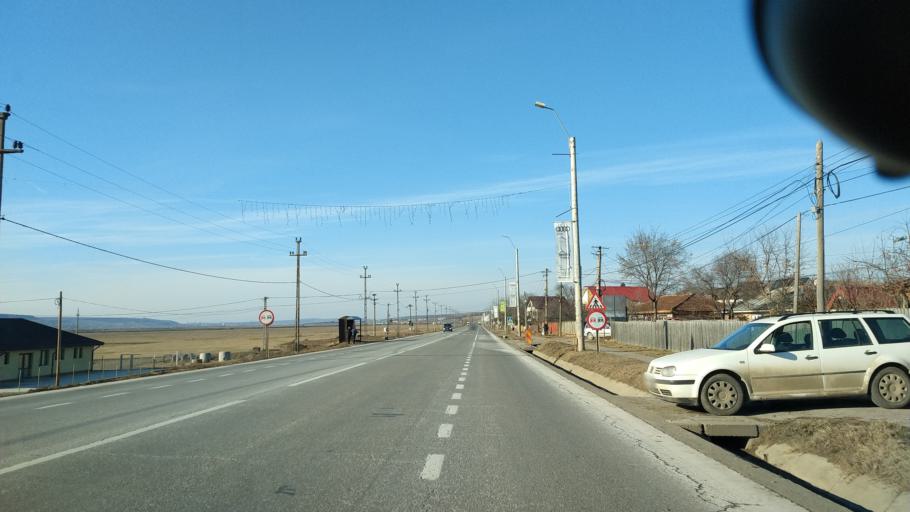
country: RO
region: Iasi
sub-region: Comuna Letcani
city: Letcani
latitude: 47.1977
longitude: 27.3944
